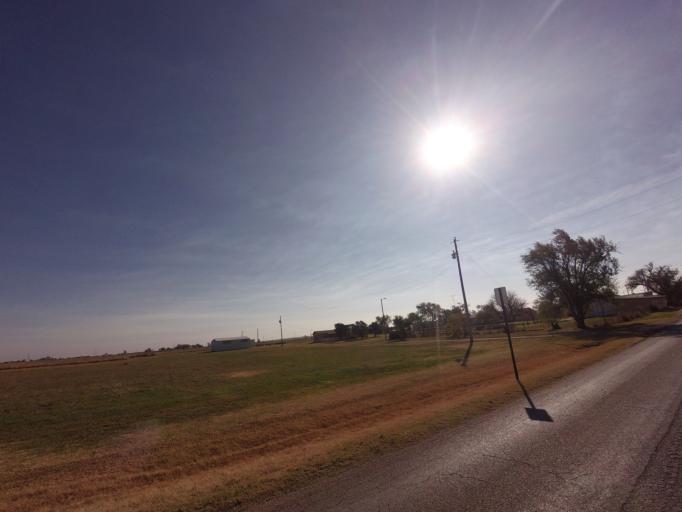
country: US
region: New Mexico
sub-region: Curry County
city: Clovis
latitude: 34.4061
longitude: -103.1611
